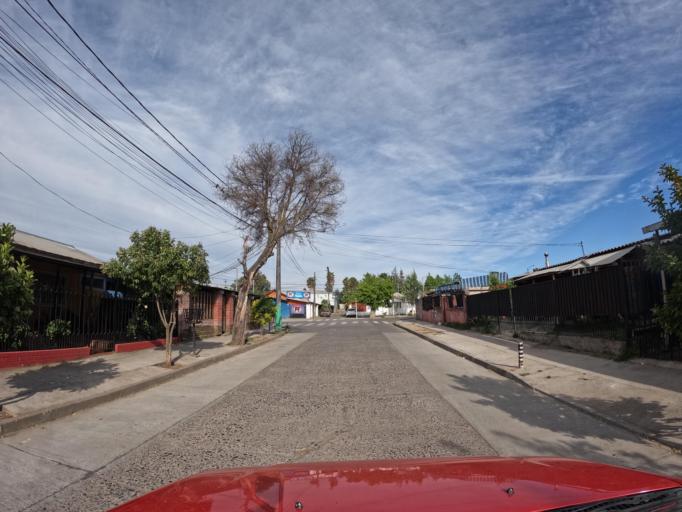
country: CL
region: Maule
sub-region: Provincia de Talca
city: Talca
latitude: -35.4417
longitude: -71.6611
